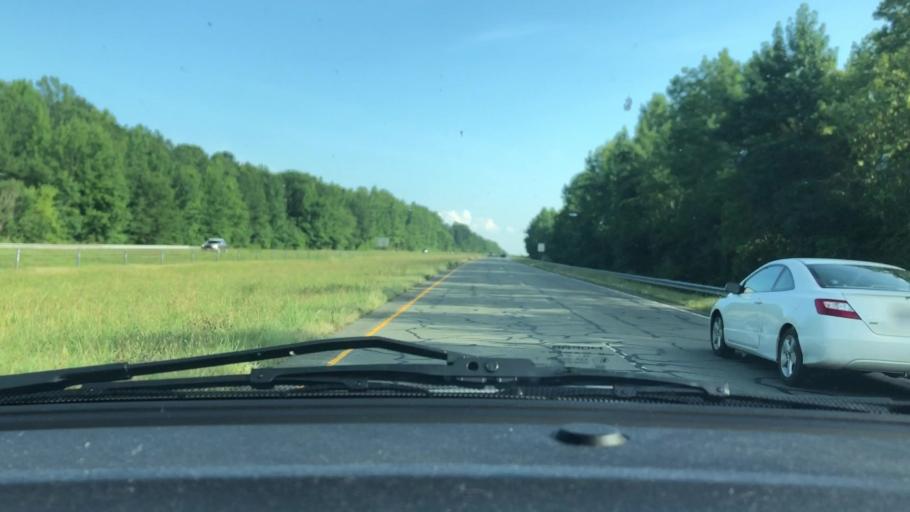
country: US
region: North Carolina
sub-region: Chatham County
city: Siler City
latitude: 35.7251
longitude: -79.4301
